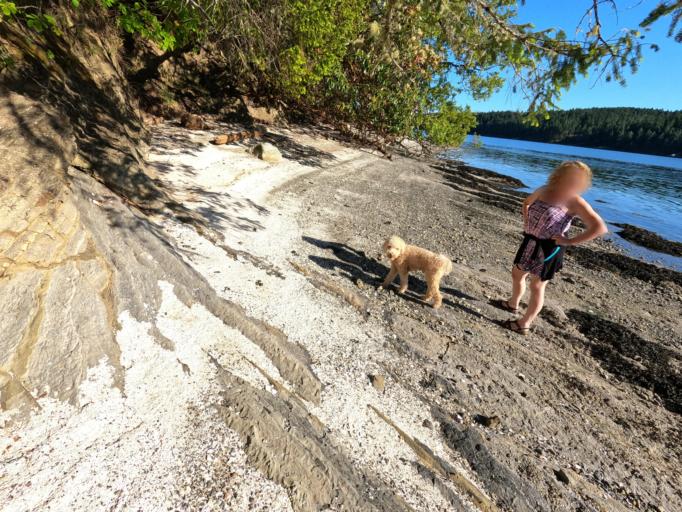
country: CA
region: British Columbia
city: North Saanich
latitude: 48.8940
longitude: -123.4070
